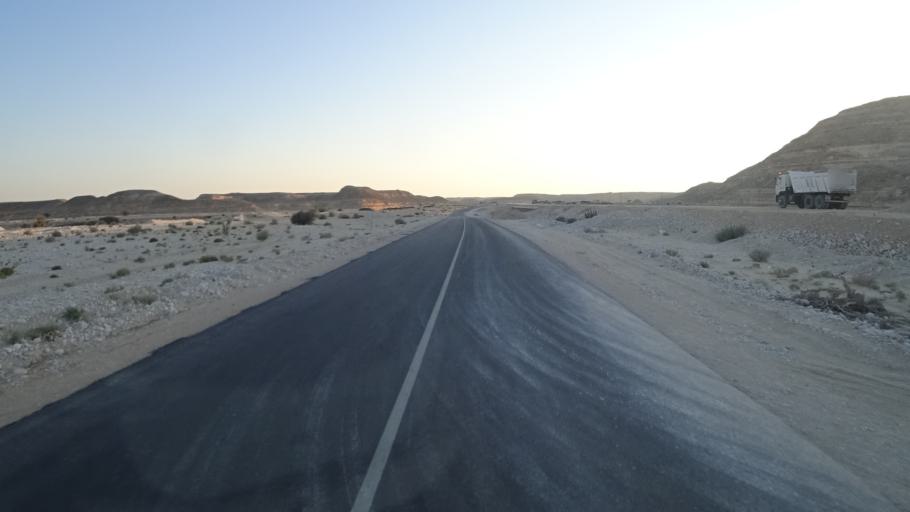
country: OM
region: Zufar
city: Salalah
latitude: 17.5190
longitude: 53.3758
